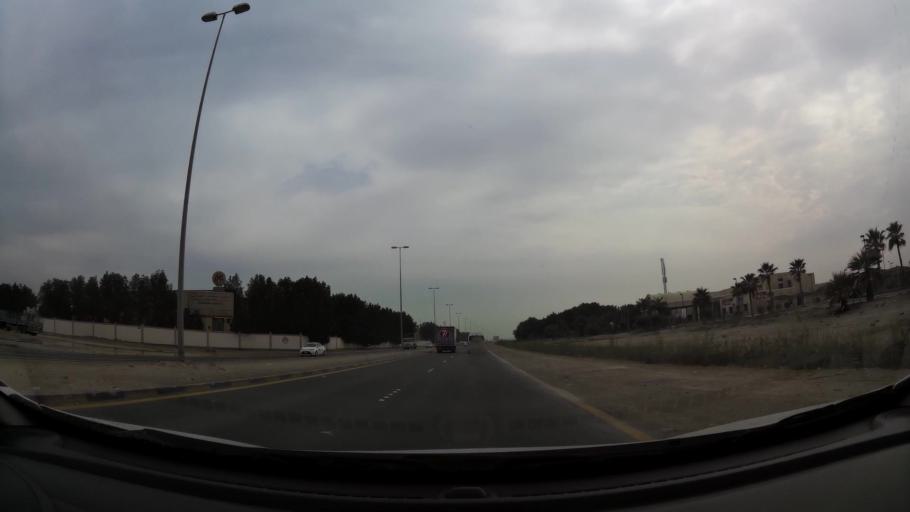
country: BH
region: Northern
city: Sitrah
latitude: 26.0849
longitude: 50.6120
